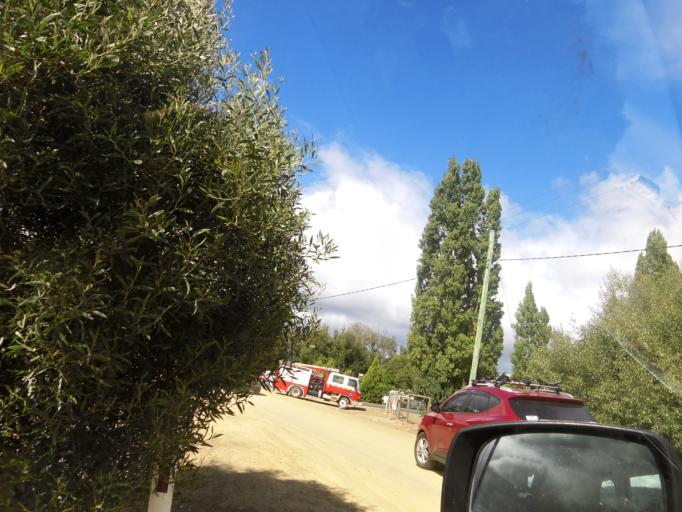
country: AU
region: Tasmania
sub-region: Huon Valley
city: Huonville
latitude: -43.0065
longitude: 147.0414
